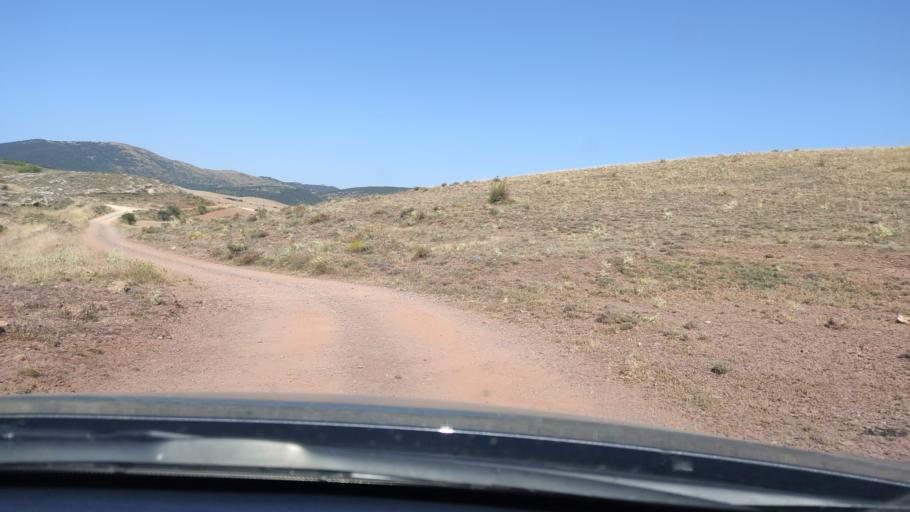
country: ES
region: Aragon
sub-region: Provincia de Teruel
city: Monforte de Moyuela
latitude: 41.0542
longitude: -1.0210
